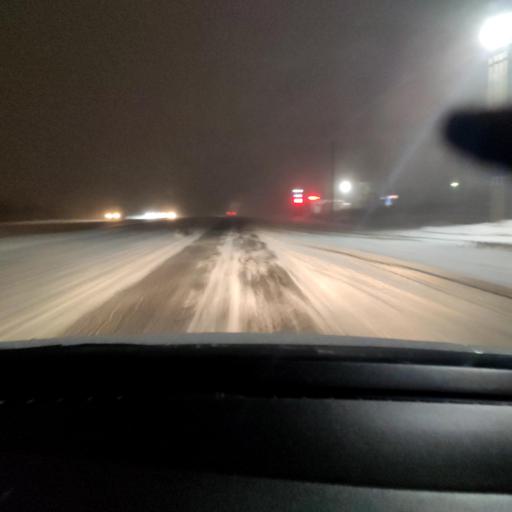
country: RU
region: Tatarstan
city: Yelabuga
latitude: 55.8141
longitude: 52.0426
